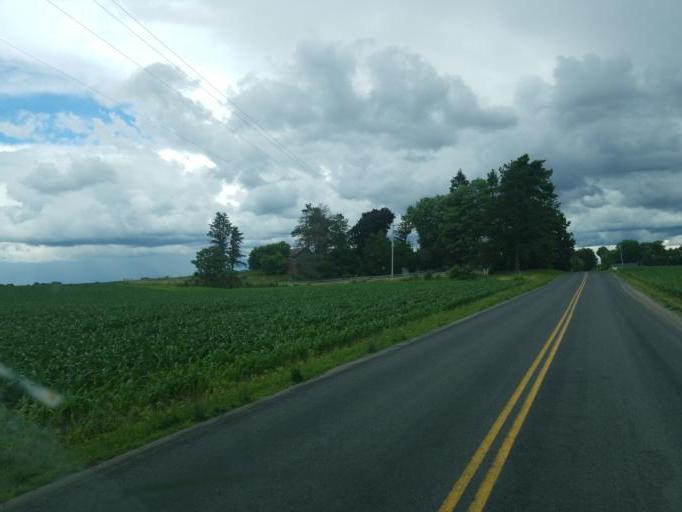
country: US
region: New York
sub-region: Seneca County
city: Waterloo
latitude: 42.9681
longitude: -76.9446
